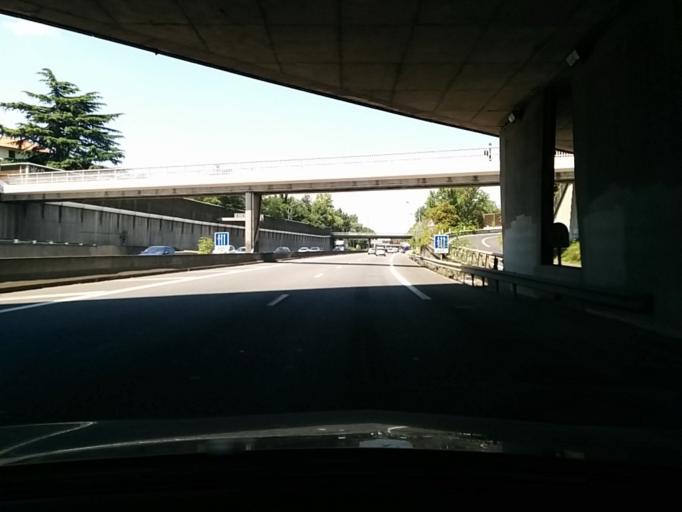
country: FR
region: Midi-Pyrenees
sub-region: Departement de la Haute-Garonne
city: Toulouse
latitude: 43.5728
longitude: 1.4525
